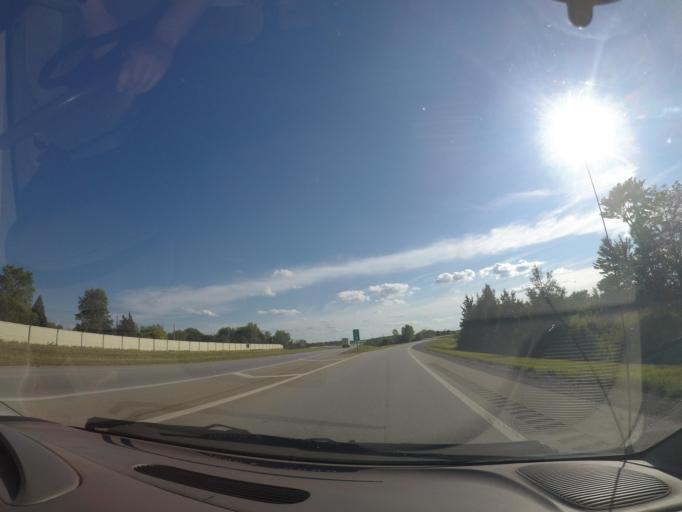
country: US
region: Ohio
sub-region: Henry County
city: Napoleon
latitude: 41.4000
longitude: -84.1436
